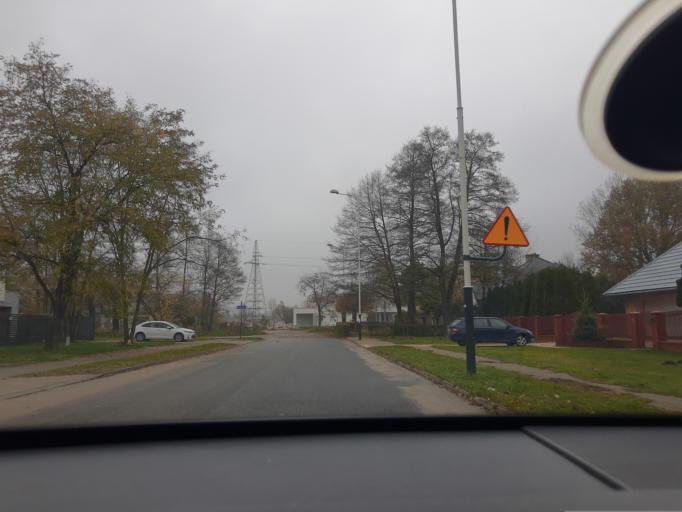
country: PL
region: Lodz Voivodeship
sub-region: Powiat pabianicki
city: Konstantynow Lodzki
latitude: 51.7467
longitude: 19.3769
